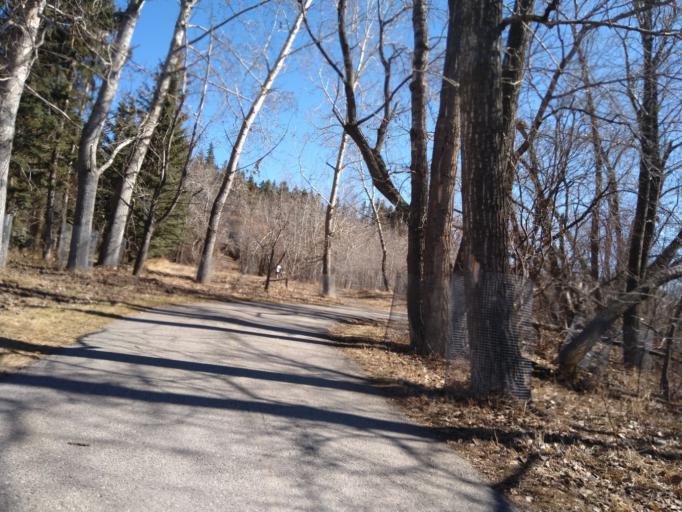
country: CA
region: Alberta
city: Calgary
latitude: 51.0232
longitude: -114.0755
